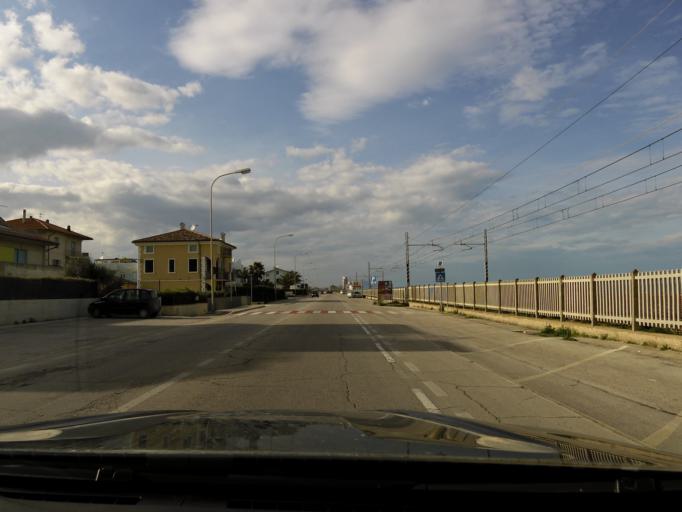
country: IT
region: The Marches
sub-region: Provincia di Macerata
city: Porto Potenza Picena
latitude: 43.3369
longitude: 13.7093
